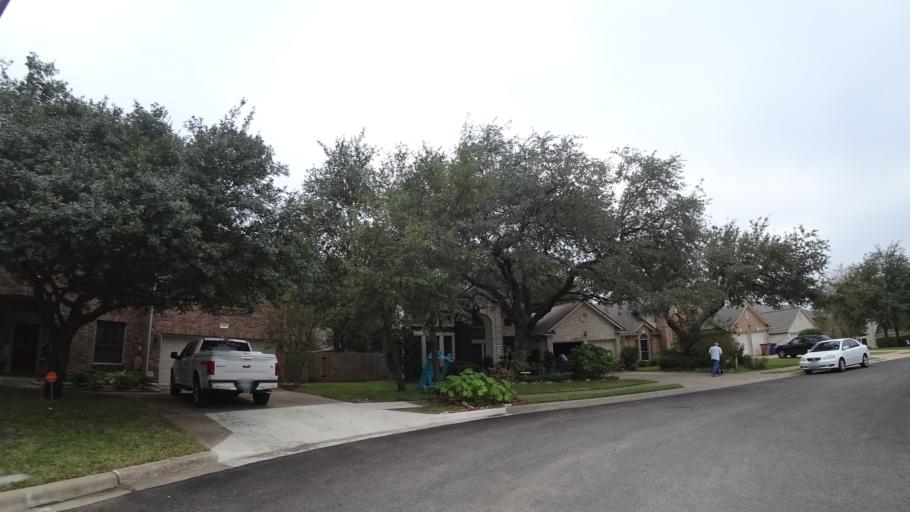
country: US
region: Texas
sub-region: Travis County
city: Shady Hollow
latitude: 30.1842
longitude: -97.8875
